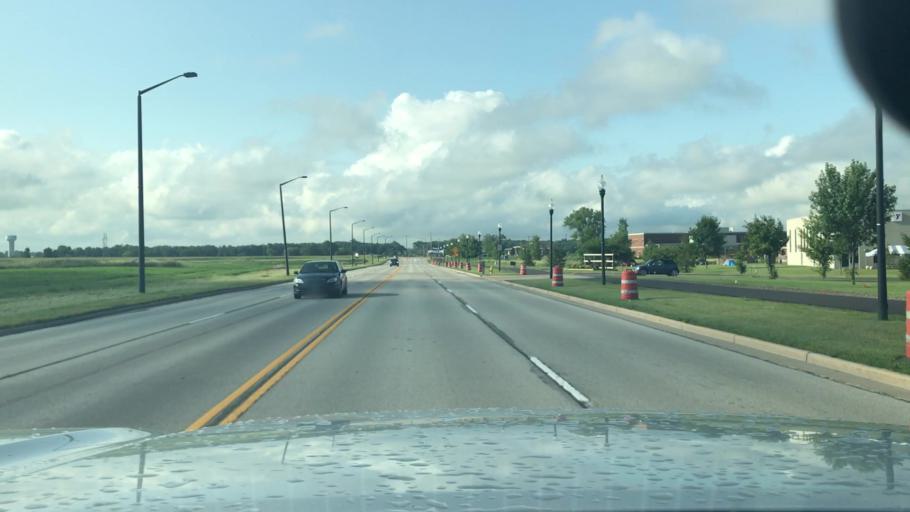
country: US
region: Wisconsin
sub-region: Brown County
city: Bellevue
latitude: 44.4700
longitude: -87.9172
